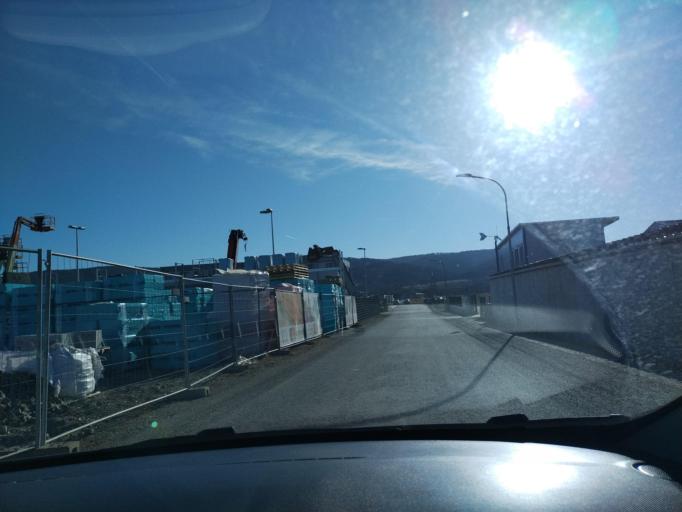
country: AT
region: Lower Austria
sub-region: Politischer Bezirk Wiener Neustadt
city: Lanzenkirchen
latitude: 47.7568
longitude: 16.2463
